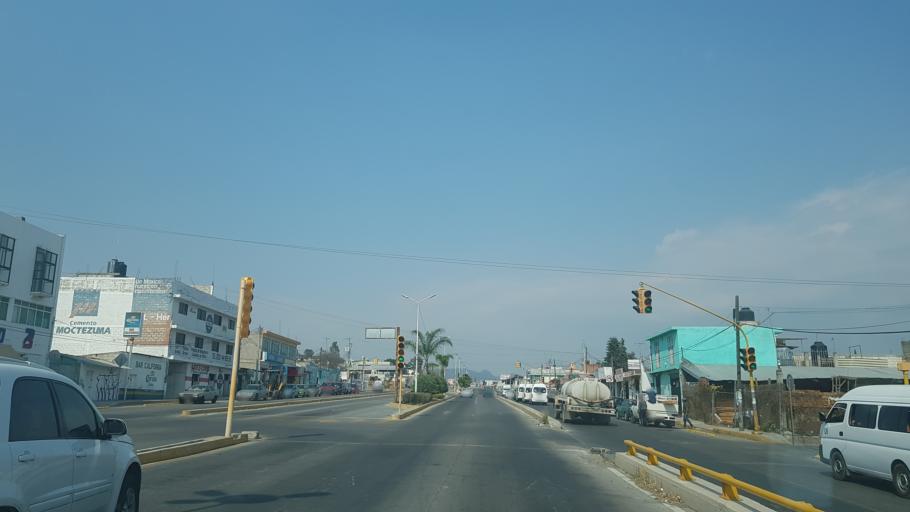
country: MX
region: Puebla
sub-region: Atlixco
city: El Encanto del Cerril
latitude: 18.9181
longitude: -98.4219
